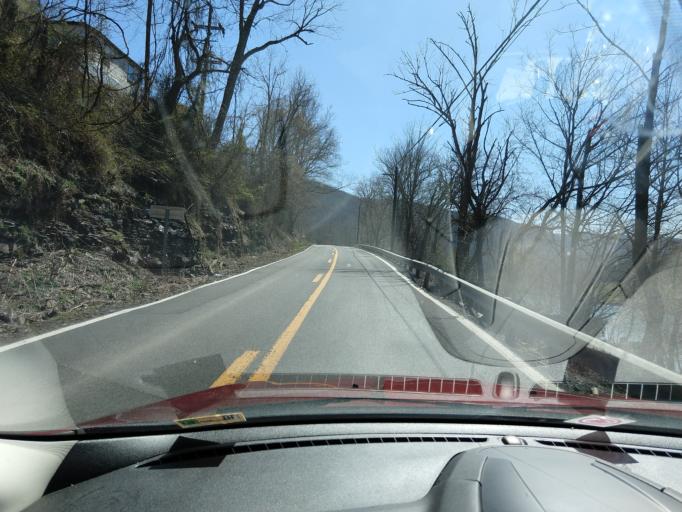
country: US
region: West Virginia
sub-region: Summers County
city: Hinton
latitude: 37.7717
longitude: -80.8914
